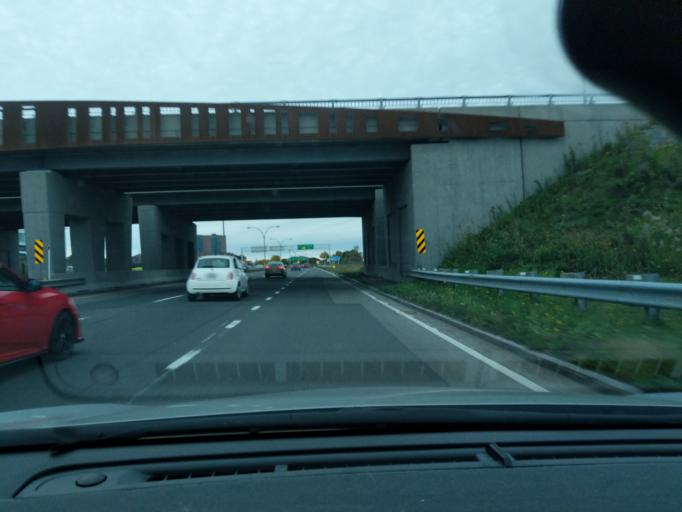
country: CA
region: Quebec
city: L'Ancienne-Lorette
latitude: 46.7655
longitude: -71.3137
